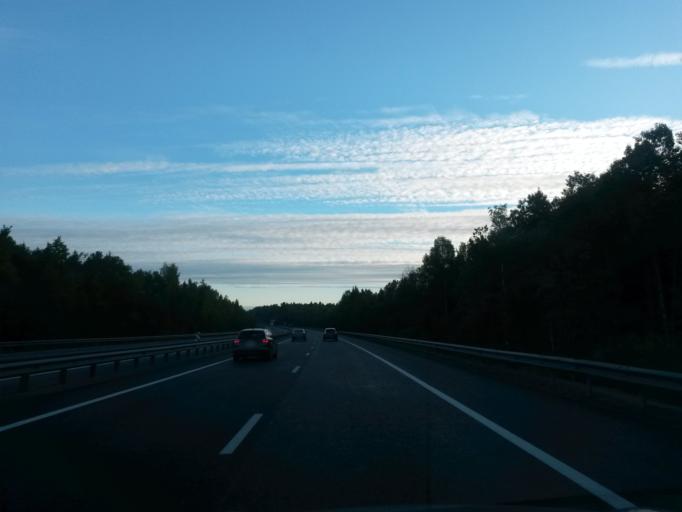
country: RU
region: Moskovskaya
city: Krasnozavodsk
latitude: 56.4349
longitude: 38.3454
